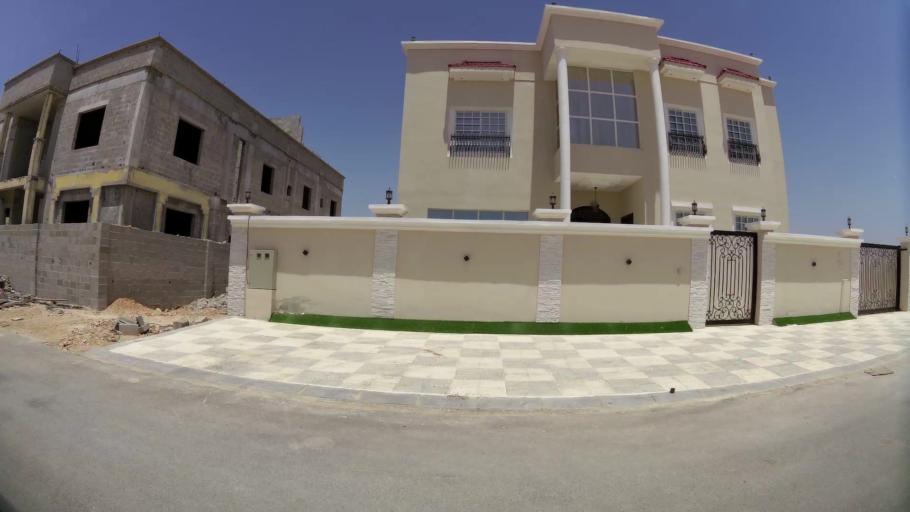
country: OM
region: Zufar
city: Salalah
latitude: 17.0850
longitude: 54.1863
